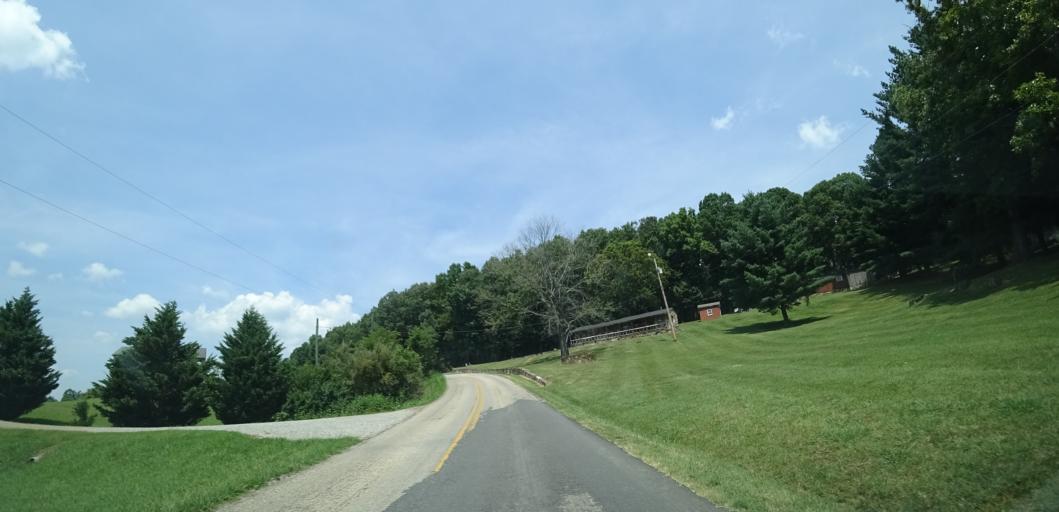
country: US
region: Virginia
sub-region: Botetourt County
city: Fincastle
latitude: 37.4737
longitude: -79.8451
